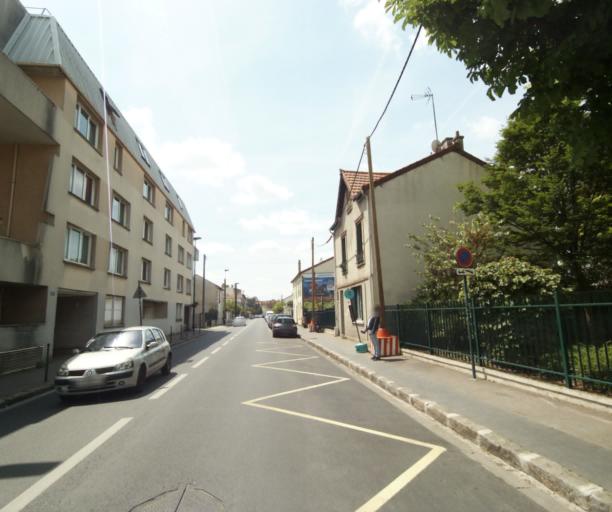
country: FR
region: Ile-de-France
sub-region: Departement des Hauts-de-Seine
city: Colombes
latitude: 48.9199
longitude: 2.2425
